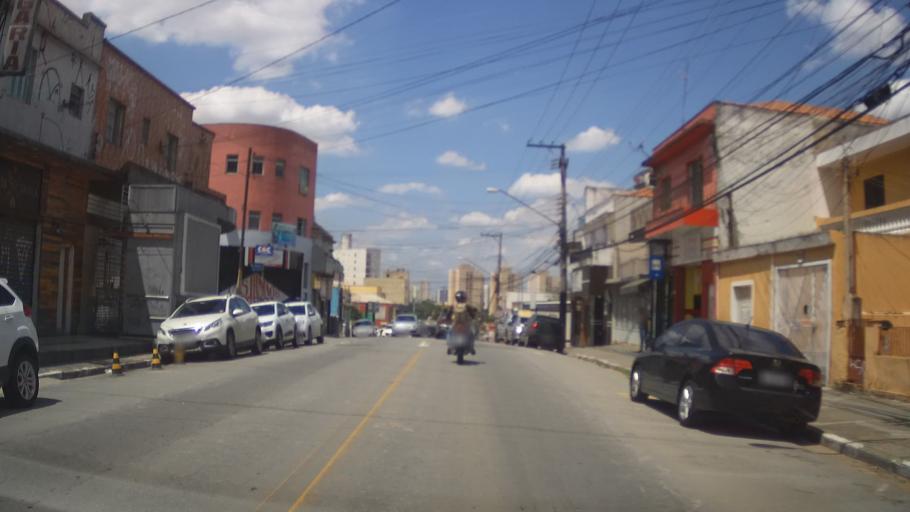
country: BR
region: Sao Paulo
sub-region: Guarulhos
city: Guarulhos
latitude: -23.4804
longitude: -46.5399
